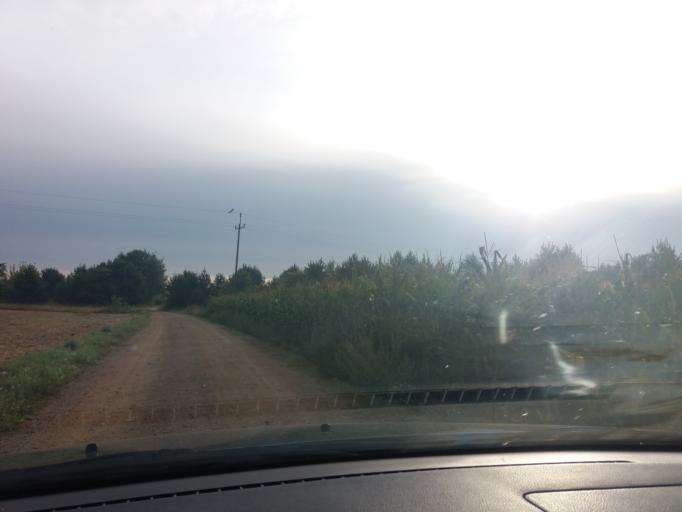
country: PL
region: Masovian Voivodeship
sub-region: Powiat mlawski
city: Wieczfnia Koscielna
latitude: 53.2021
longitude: 20.4415
